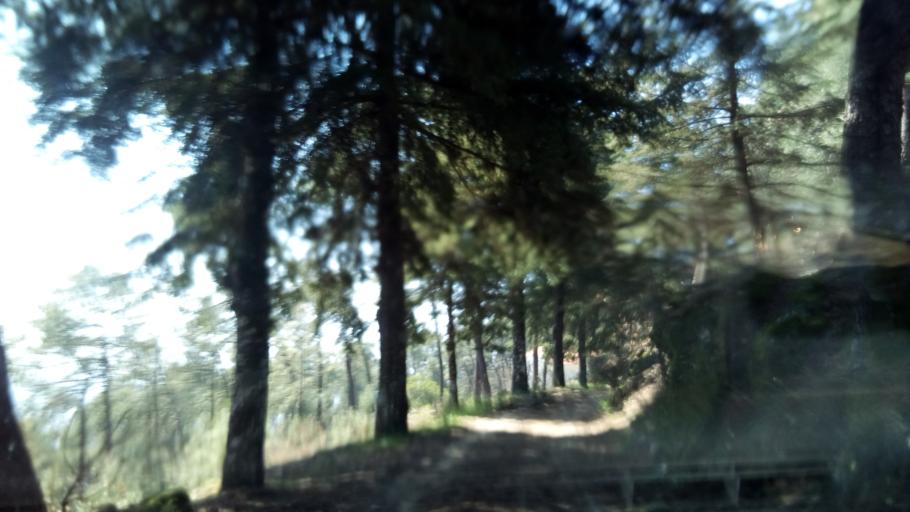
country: PT
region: Guarda
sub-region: Fornos de Algodres
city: Fornos de Algodres
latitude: 40.6240
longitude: -7.5418
